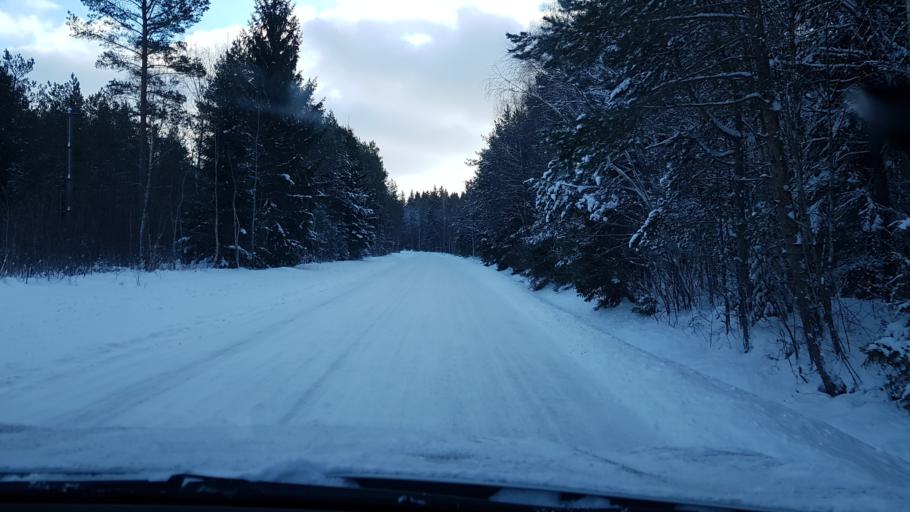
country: EE
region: Harju
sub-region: Nissi vald
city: Turba
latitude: 59.1589
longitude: 24.1441
